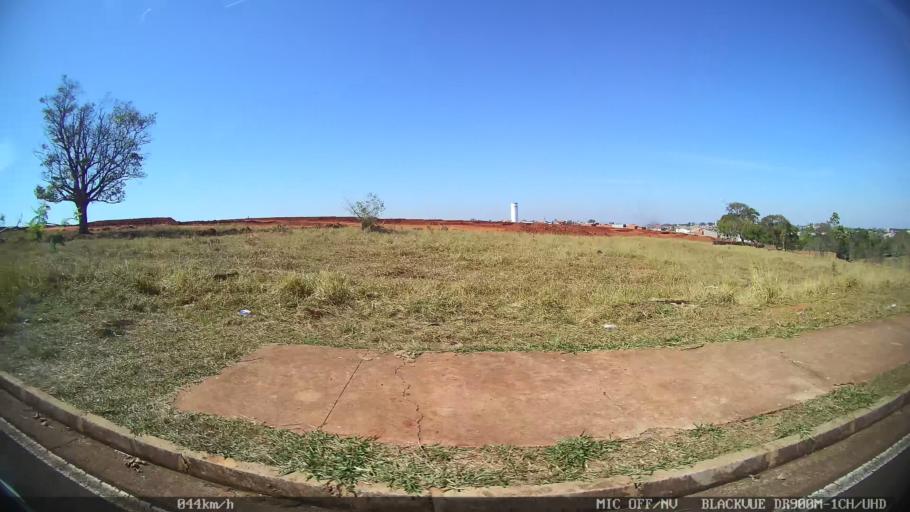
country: BR
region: Sao Paulo
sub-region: Sao Jose Do Rio Preto
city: Sao Jose do Rio Preto
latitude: -20.7523
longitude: -49.4226
